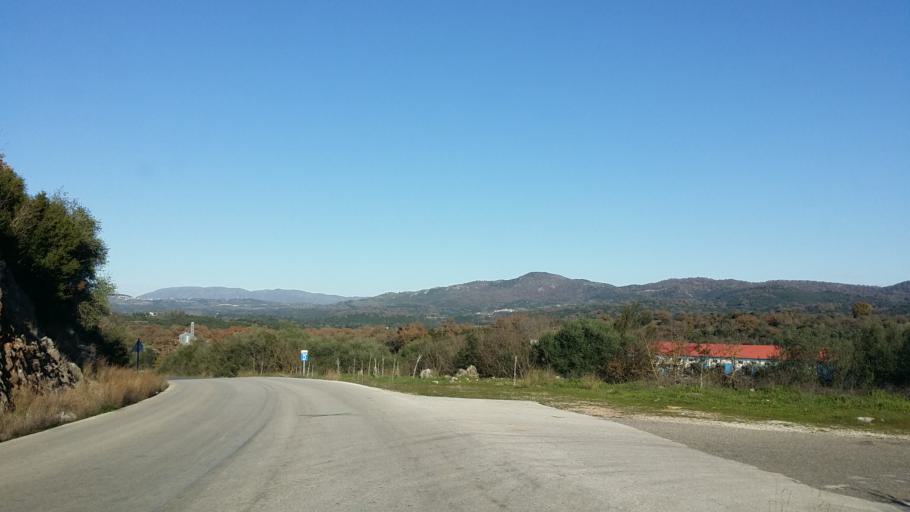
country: GR
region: West Greece
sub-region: Nomos Aitolias kai Akarnanias
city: Astakos
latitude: 38.6128
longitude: 21.1402
